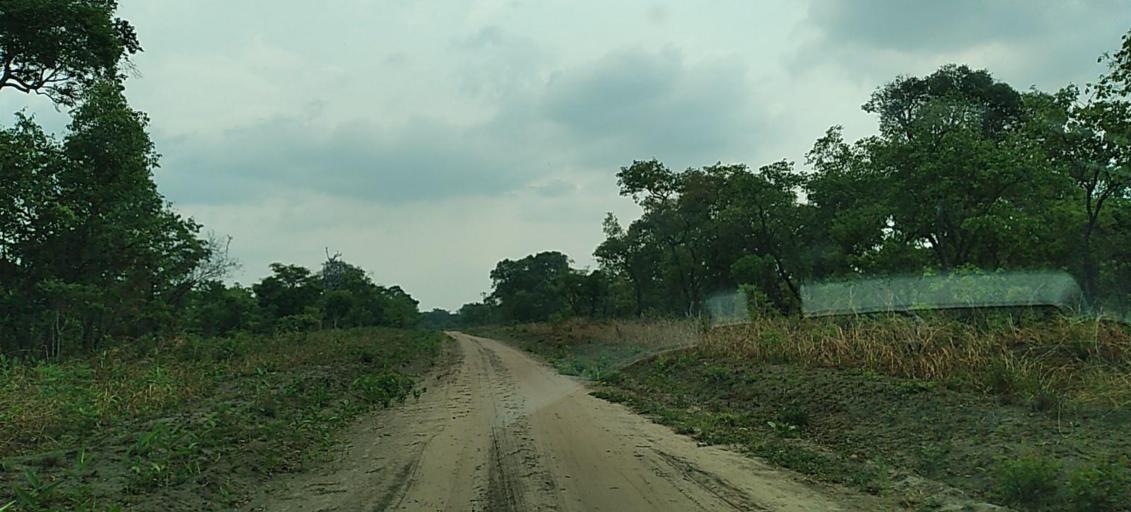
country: ZM
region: North-Western
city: Mwinilunga
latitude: -11.4068
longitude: 24.6262
